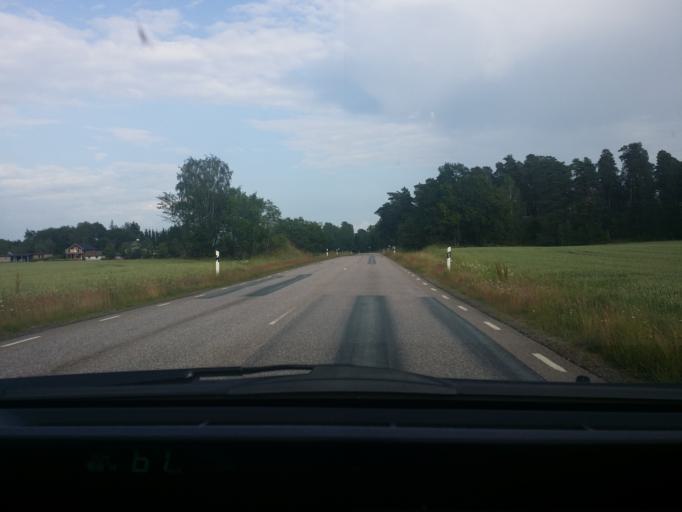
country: SE
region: Vaestmanland
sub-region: Hallstahammars Kommun
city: Kolback
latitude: 59.5635
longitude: 16.2588
